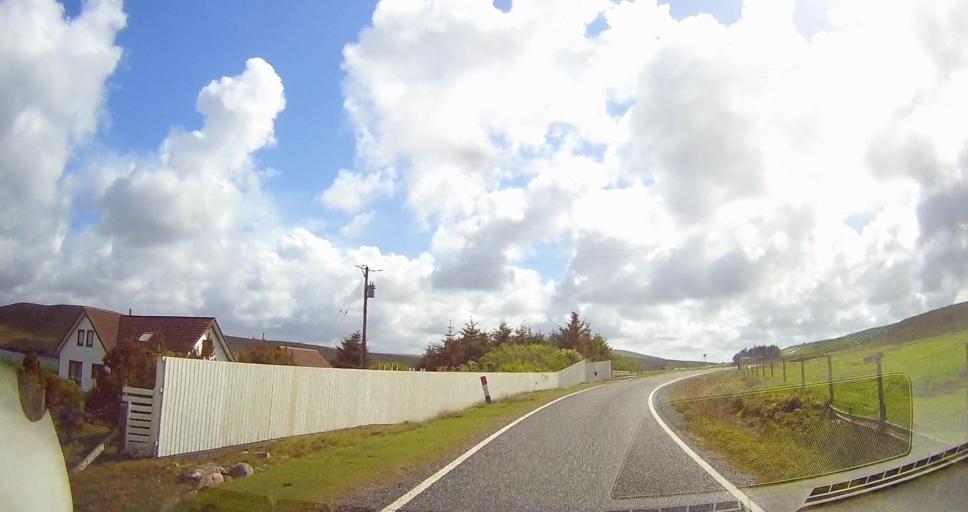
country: GB
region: Scotland
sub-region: Shetland Islands
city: Lerwick
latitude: 60.5364
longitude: -1.3564
